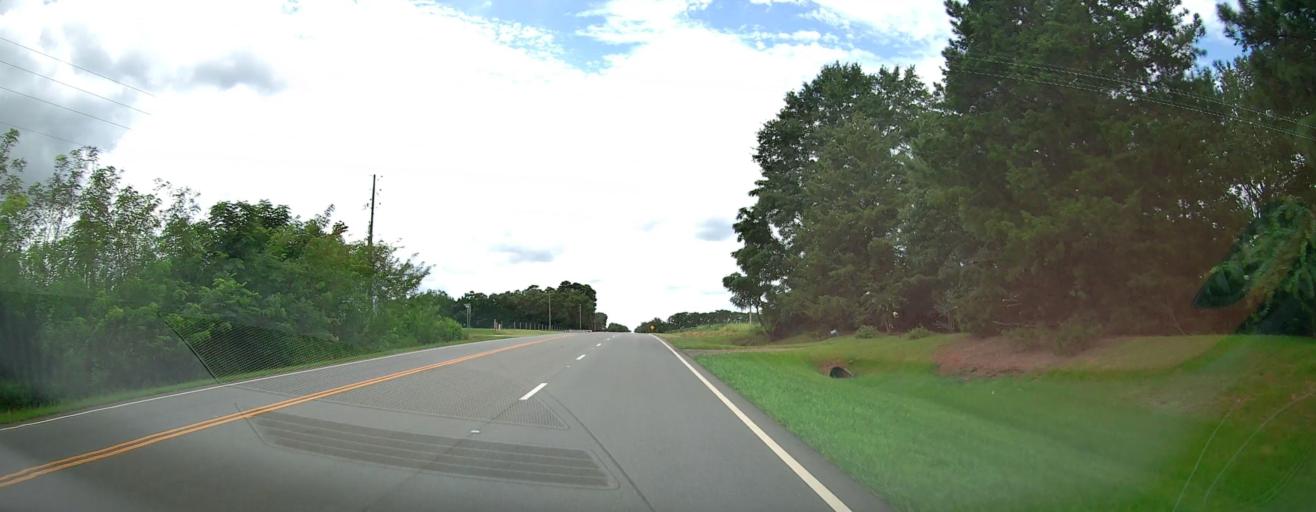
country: US
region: Georgia
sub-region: Macon County
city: Montezuma
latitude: 32.2930
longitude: -83.9511
